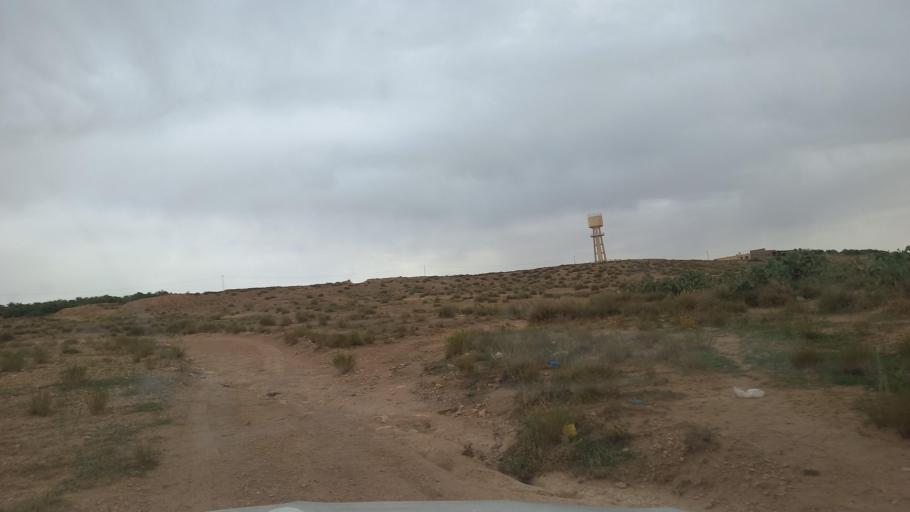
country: TN
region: Al Qasrayn
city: Sbiba
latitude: 35.3829
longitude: 9.0641
